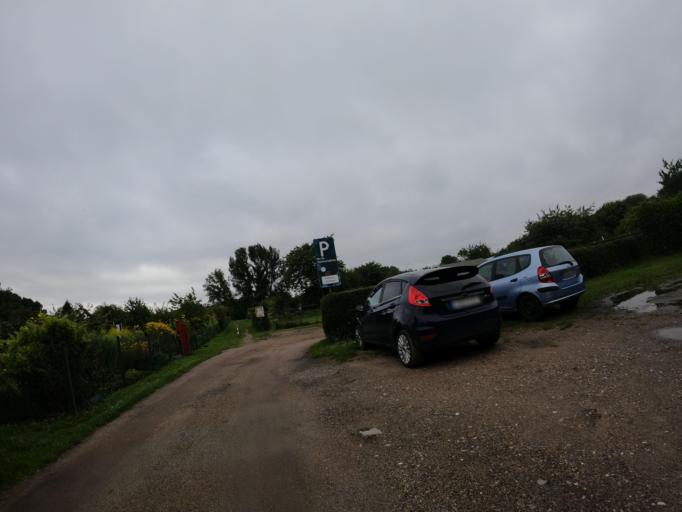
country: DE
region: Mecklenburg-Vorpommern
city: Putbus
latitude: 54.3564
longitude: 13.4663
